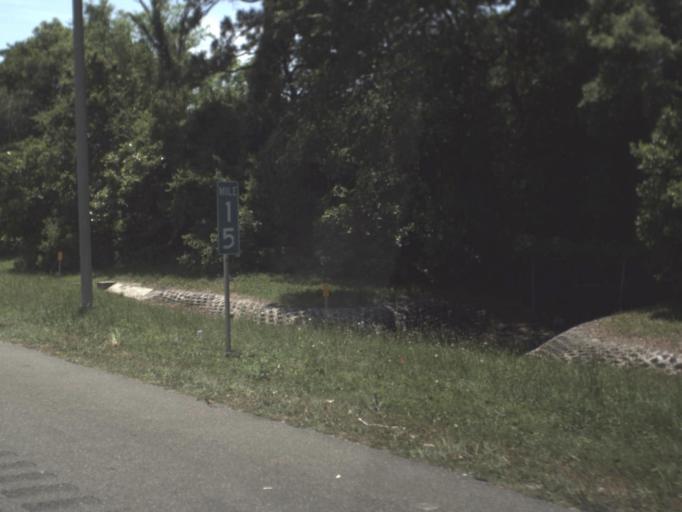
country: US
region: Florida
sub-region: Clay County
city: Bellair-Meadowbrook Terrace
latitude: 30.2335
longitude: -81.7631
